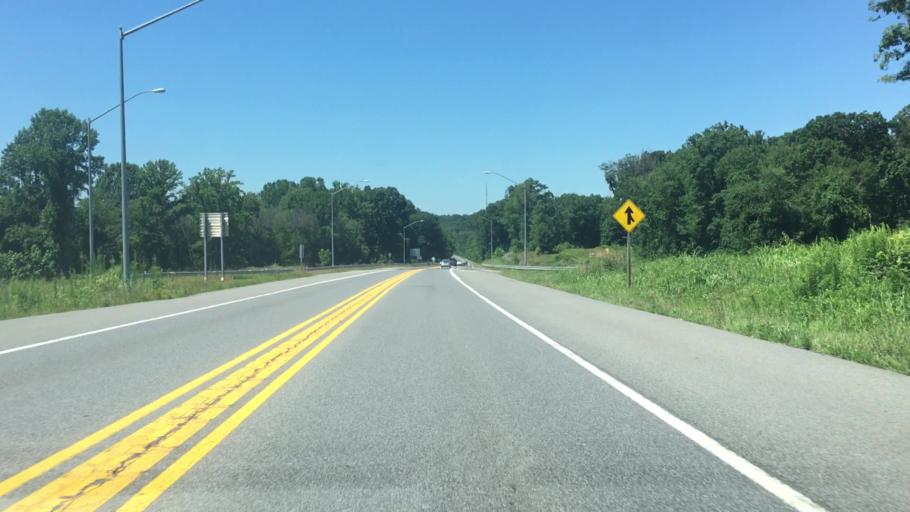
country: US
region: Maryland
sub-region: Howard County
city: Highland
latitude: 39.2308
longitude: -76.9737
